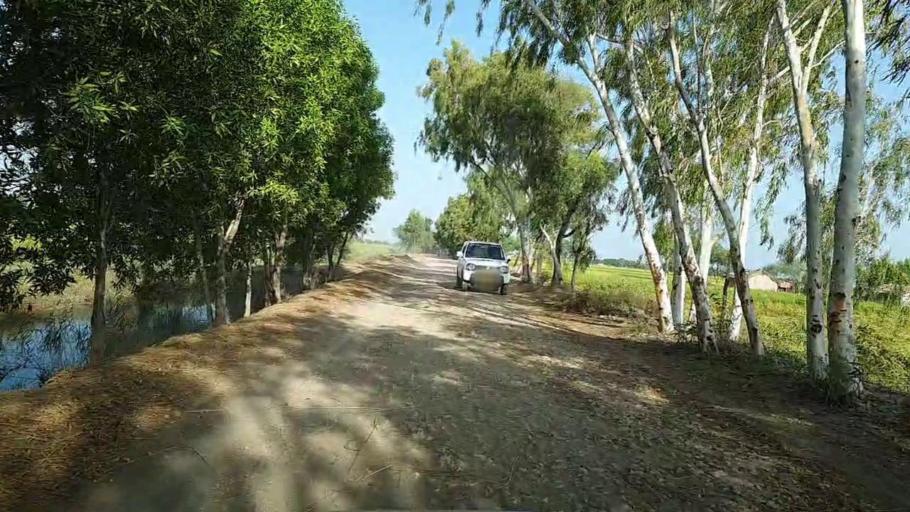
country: PK
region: Sindh
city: Kario
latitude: 24.5996
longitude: 68.5137
